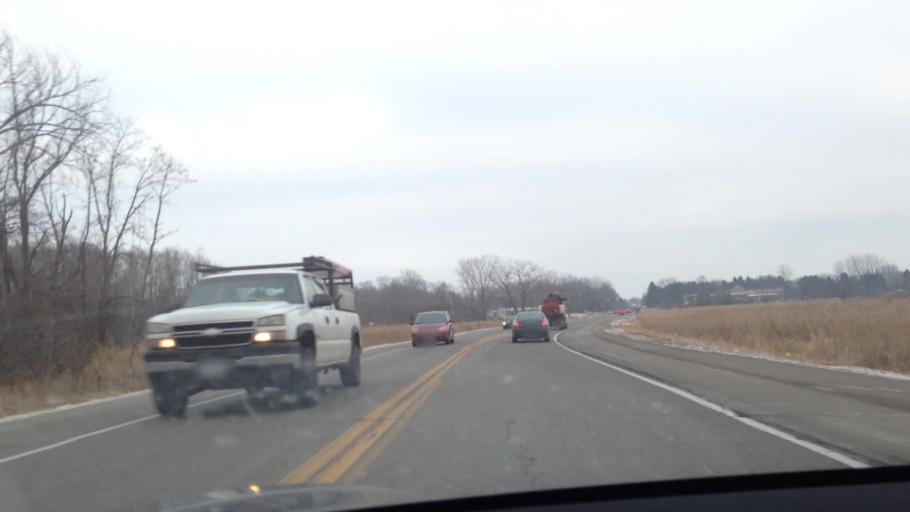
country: US
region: Minnesota
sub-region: Anoka County
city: Columbus
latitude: 45.2518
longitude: -93.0152
